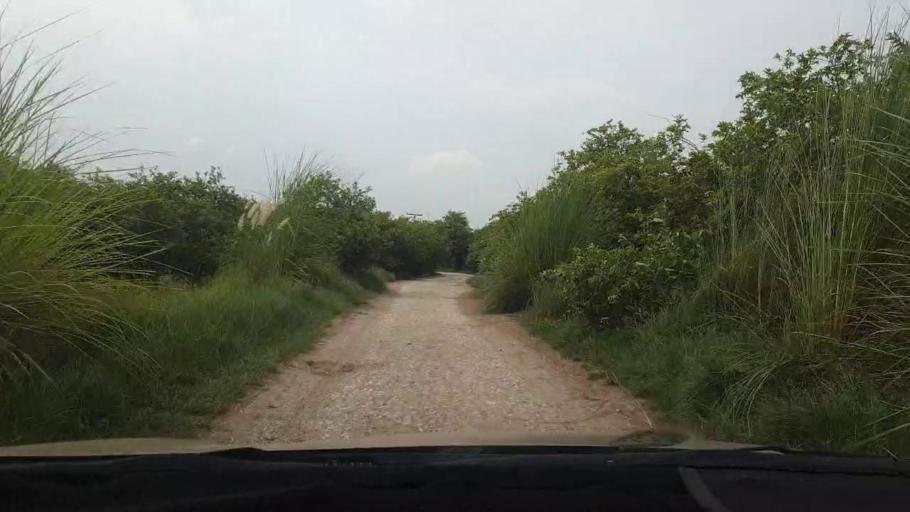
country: PK
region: Sindh
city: Naudero
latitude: 27.6325
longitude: 68.3093
